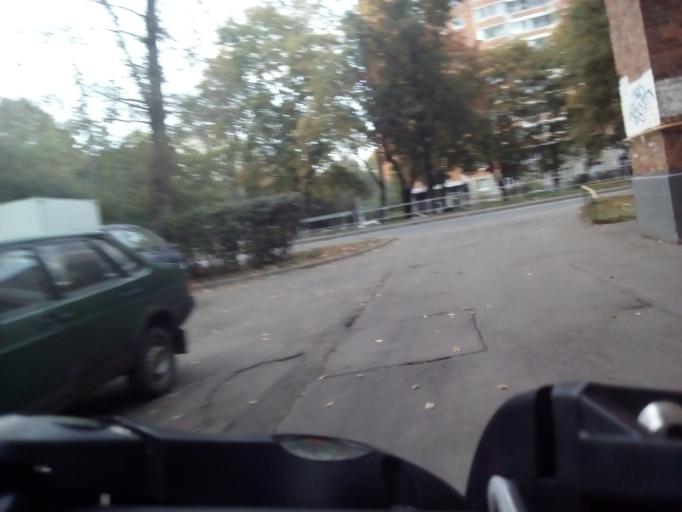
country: RU
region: Moscow
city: Sviblovo
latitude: 55.8513
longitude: 37.6393
